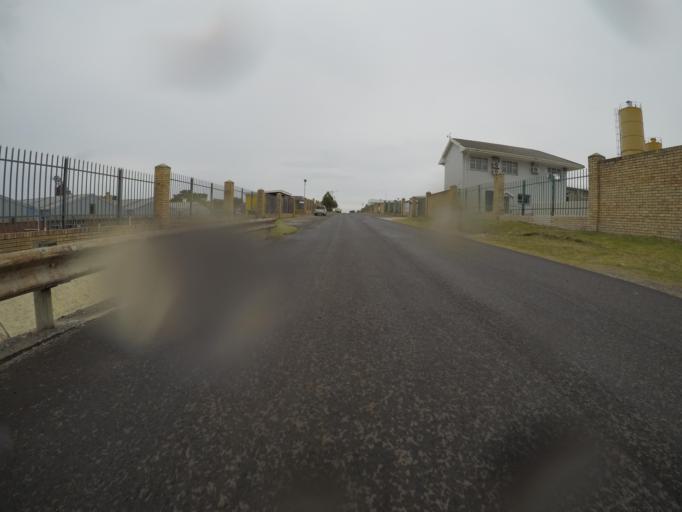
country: ZA
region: Eastern Cape
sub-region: Buffalo City Metropolitan Municipality
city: East London
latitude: -32.9762
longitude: 27.8239
